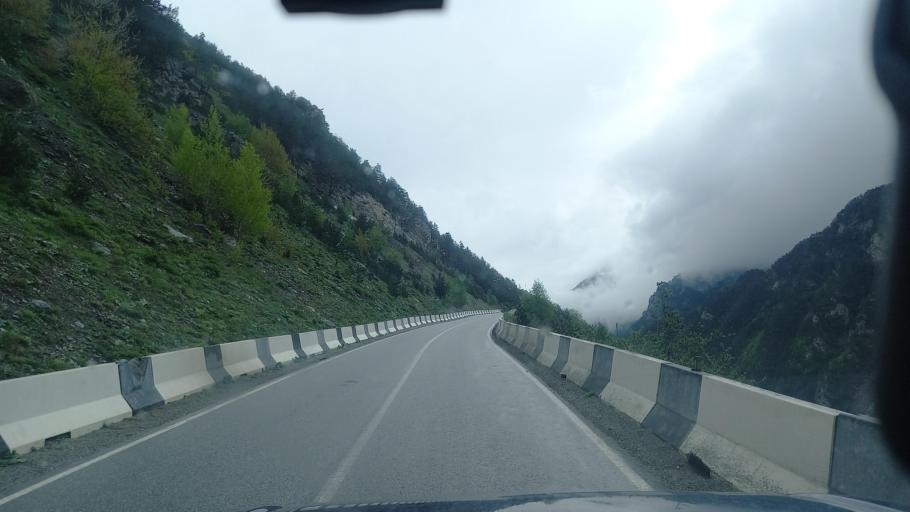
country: RU
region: North Ossetia
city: Mizur
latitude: 42.7930
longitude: 44.0002
